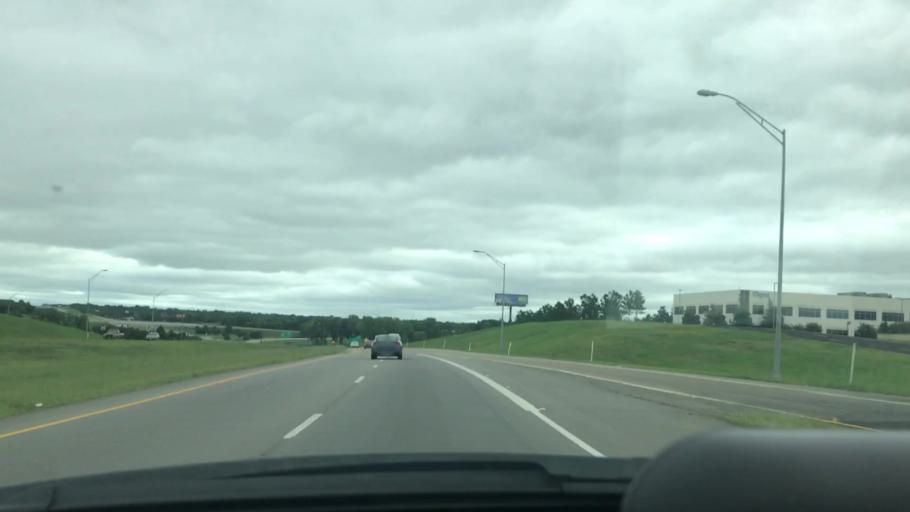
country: US
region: Texas
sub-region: Grayson County
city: Denison
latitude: 33.7119
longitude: -96.5867
